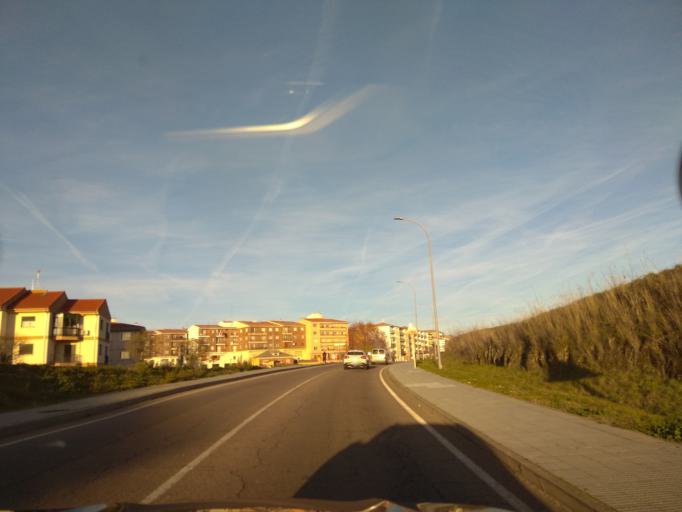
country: ES
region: Castille and Leon
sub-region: Provincia de Salamanca
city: Ciudad Rodrigo
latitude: 40.6000
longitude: -6.5383
